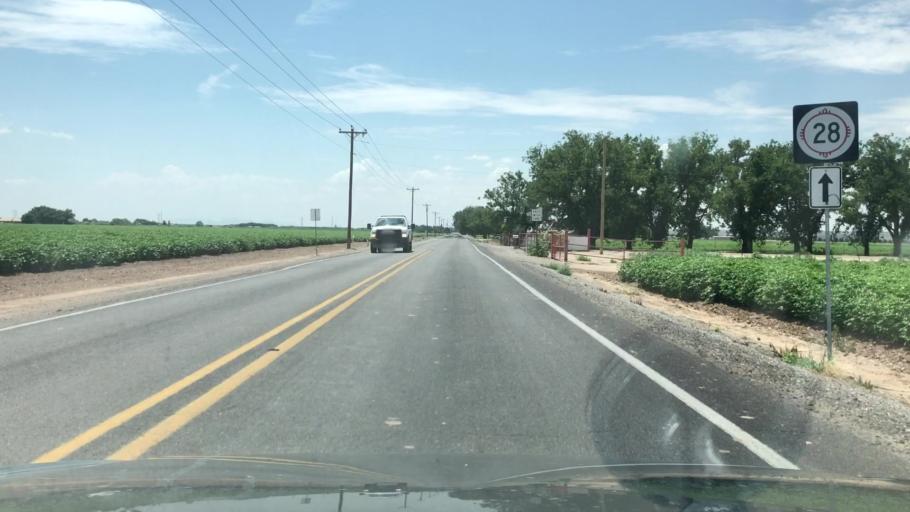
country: US
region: New Mexico
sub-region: Dona Ana County
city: Vado
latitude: 32.1102
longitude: -106.6836
